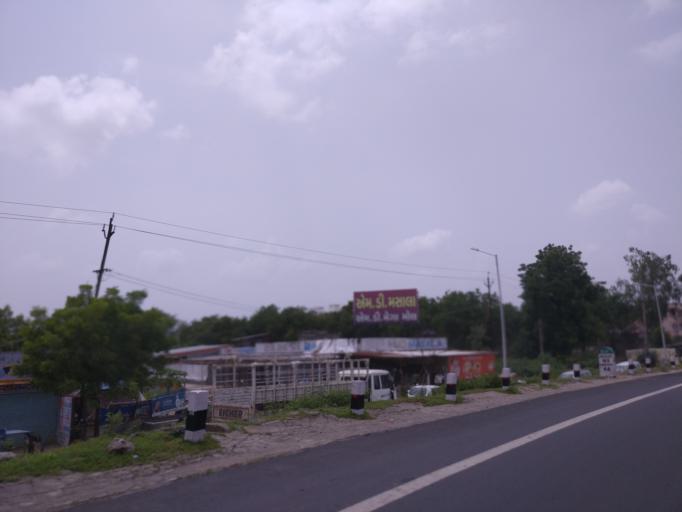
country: IN
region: Gujarat
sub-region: Mahesana
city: Jhulasan
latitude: 23.2423
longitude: 72.4871
